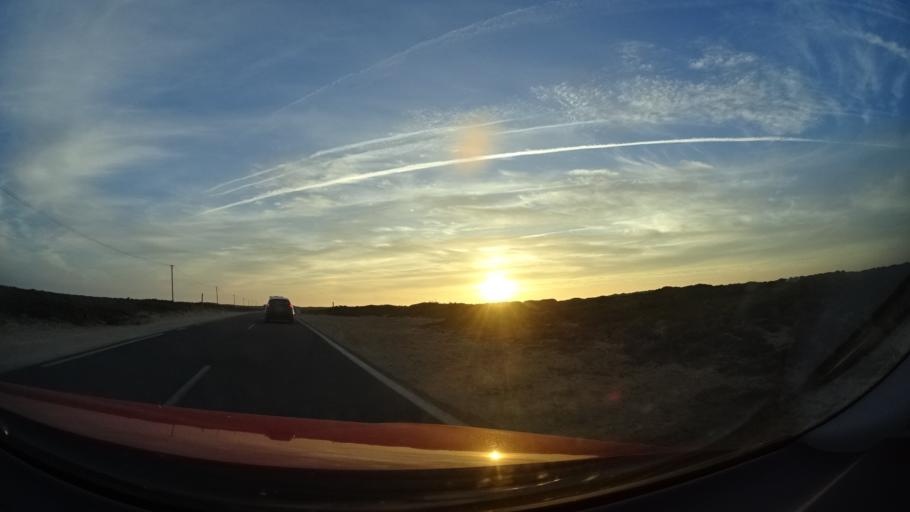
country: PT
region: Faro
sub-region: Vila do Bispo
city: Sagres
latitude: 37.0274
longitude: -8.9859
